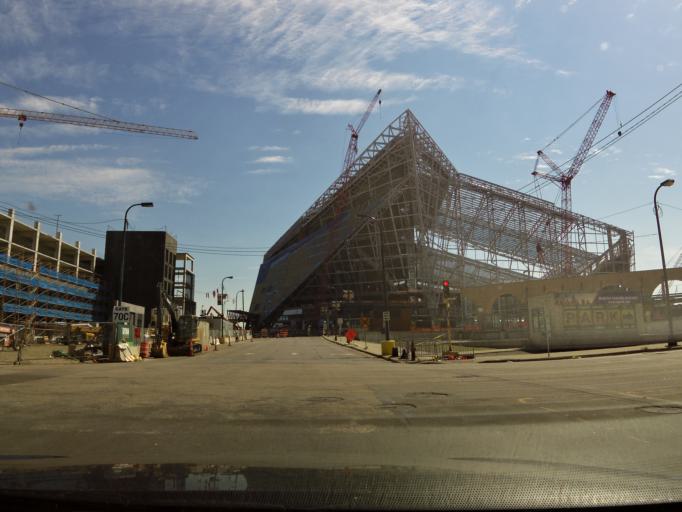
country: US
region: Minnesota
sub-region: Hennepin County
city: Minneapolis
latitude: 44.9758
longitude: -93.2605
